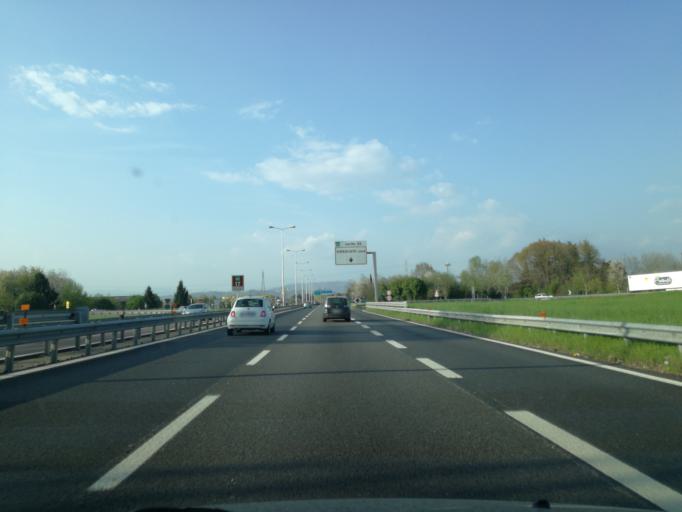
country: IT
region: Lombardy
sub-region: Provincia di Monza e Brianza
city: Velasca
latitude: 45.6330
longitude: 9.3630
